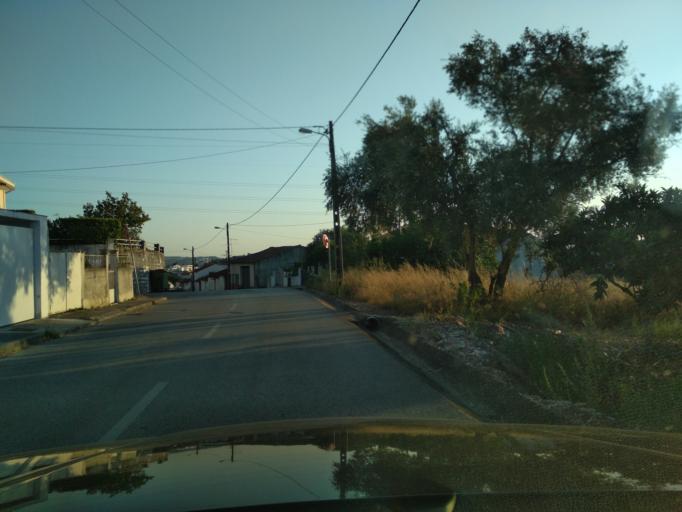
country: PT
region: Coimbra
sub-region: Coimbra
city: Coimbra
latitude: 40.2395
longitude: -8.4065
